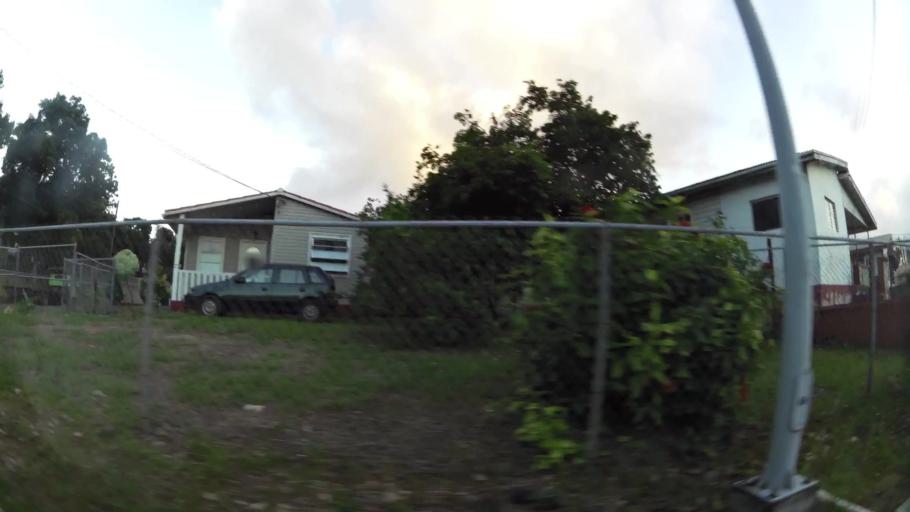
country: AG
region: Saint John
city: Saint John's
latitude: 17.1279
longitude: -61.8384
